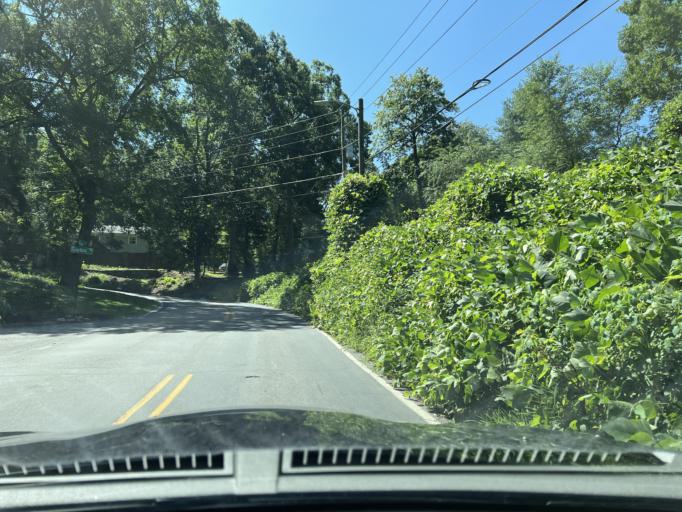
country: US
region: North Carolina
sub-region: Buncombe County
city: Biltmore Forest
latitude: 35.5706
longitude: -82.5151
